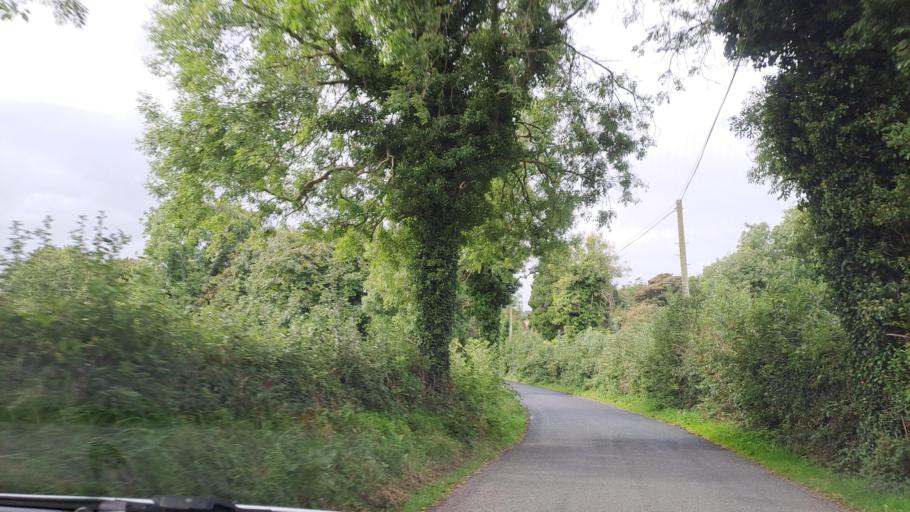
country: IE
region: Ulster
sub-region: County Monaghan
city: Carrickmacross
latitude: 53.9837
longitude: -6.7803
